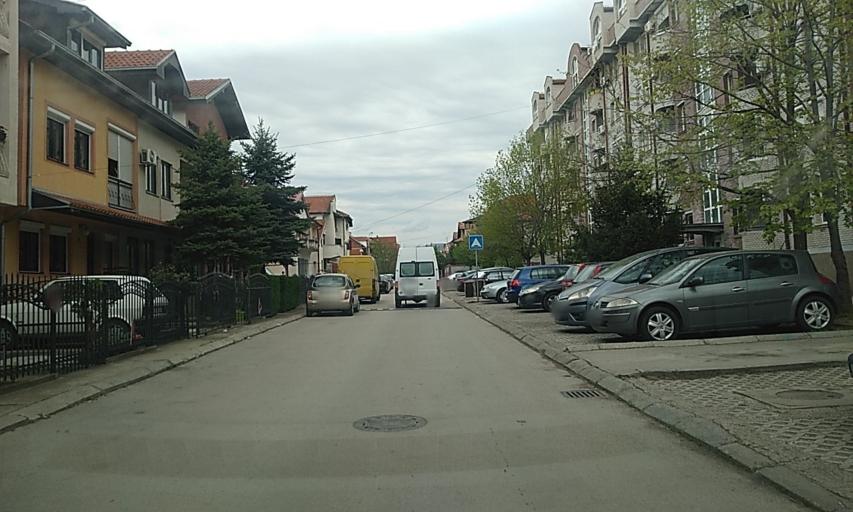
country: RS
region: Central Serbia
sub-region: Nisavski Okrug
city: Nis
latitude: 43.3313
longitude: 21.9358
